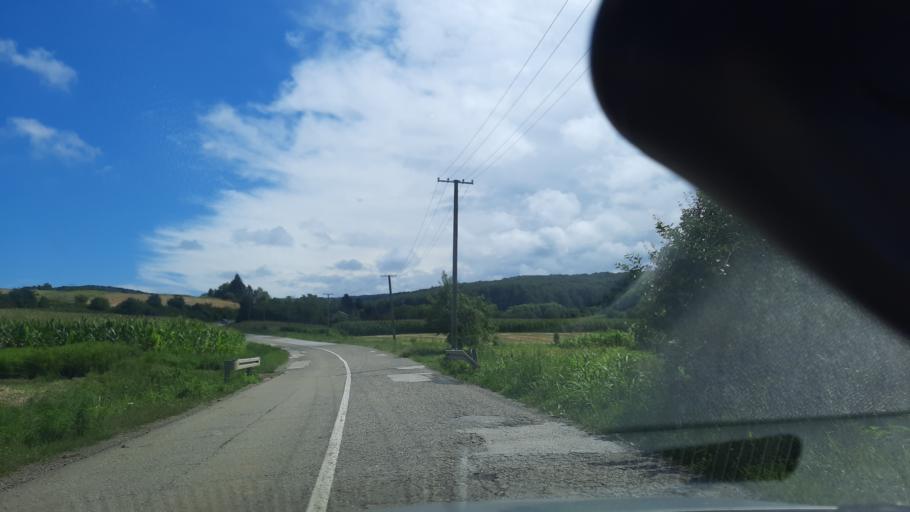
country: RS
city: Glozan
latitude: 45.1683
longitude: 19.5878
